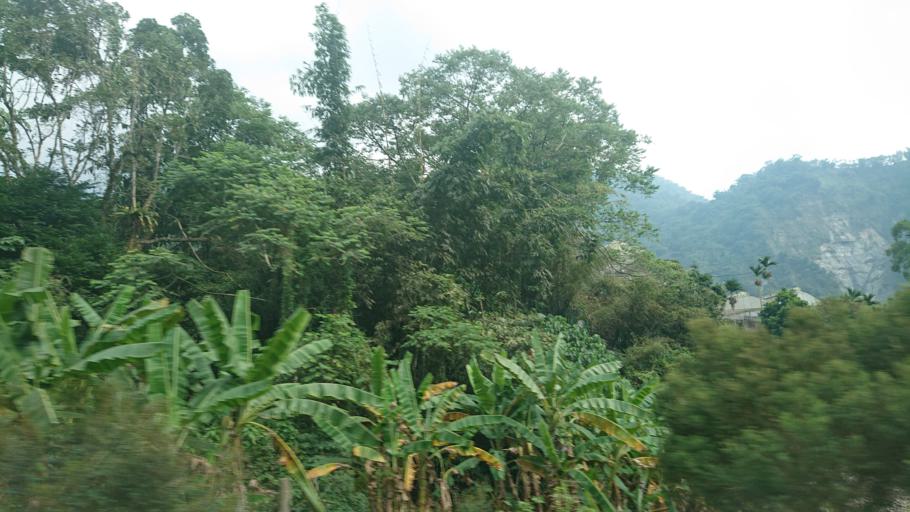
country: TW
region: Taiwan
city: Lugu
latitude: 23.5941
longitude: 120.7000
